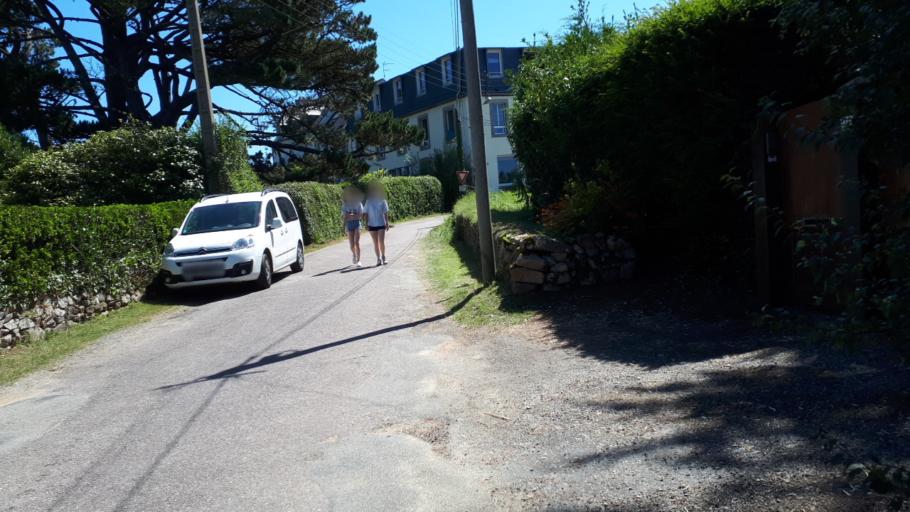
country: FR
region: Brittany
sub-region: Departement du Finistere
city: Plougasnou
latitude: 48.7061
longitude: -3.8326
